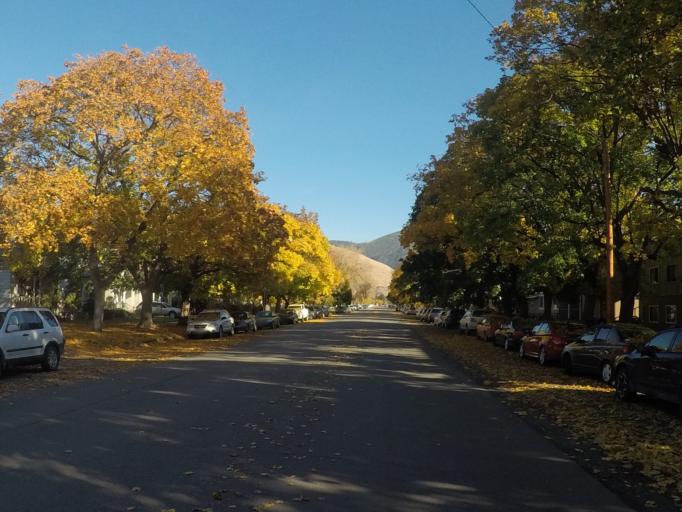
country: US
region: Montana
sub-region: Missoula County
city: Missoula
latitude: 46.8772
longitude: -113.9994
